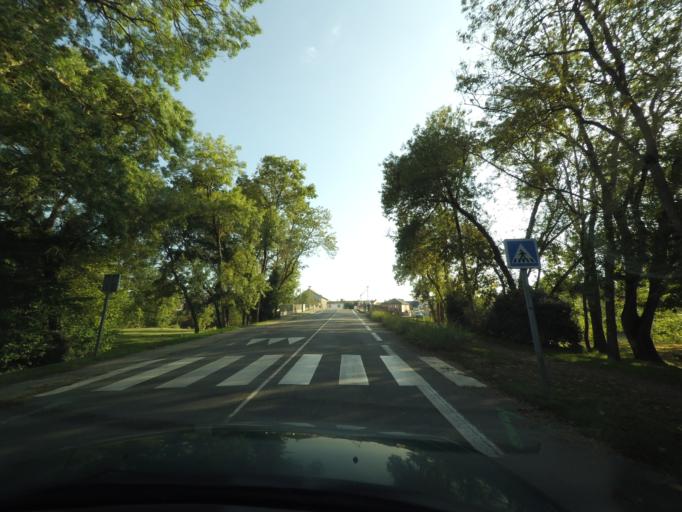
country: FR
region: Pays de la Loire
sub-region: Departement de la Loire-Atlantique
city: Saint-Philbert-de-Grand-Lieu
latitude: 47.0409
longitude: -1.6409
